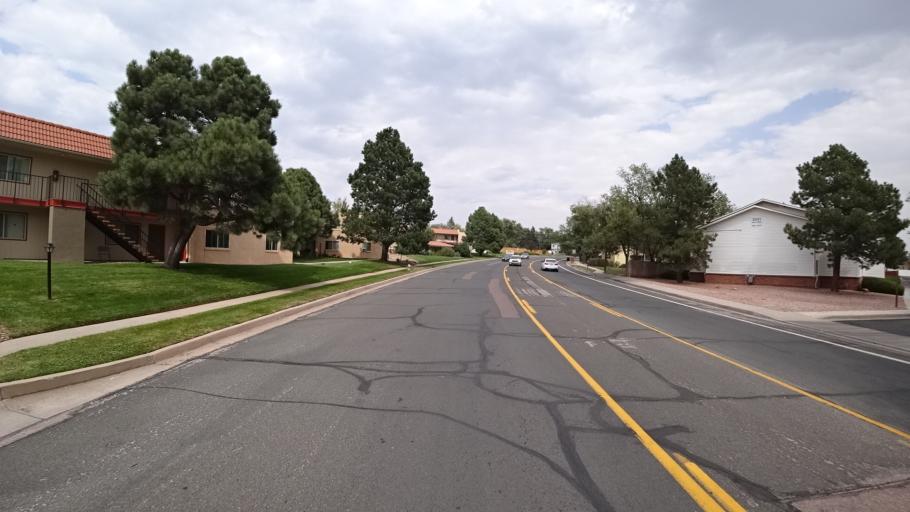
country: US
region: Colorado
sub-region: El Paso County
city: Colorado Springs
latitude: 38.8459
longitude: -104.7821
